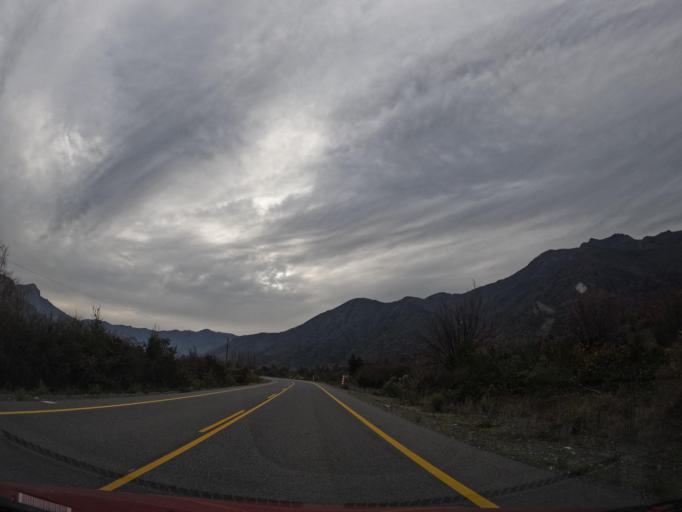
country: CL
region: Maule
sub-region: Provincia de Linares
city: Colbun
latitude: -35.7284
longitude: -71.0167
